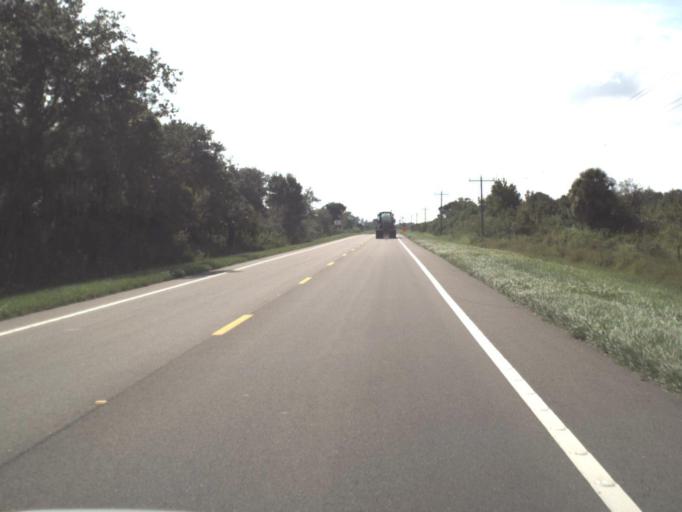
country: US
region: Florida
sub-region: Sarasota County
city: The Meadows
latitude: 27.4754
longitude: -82.3587
